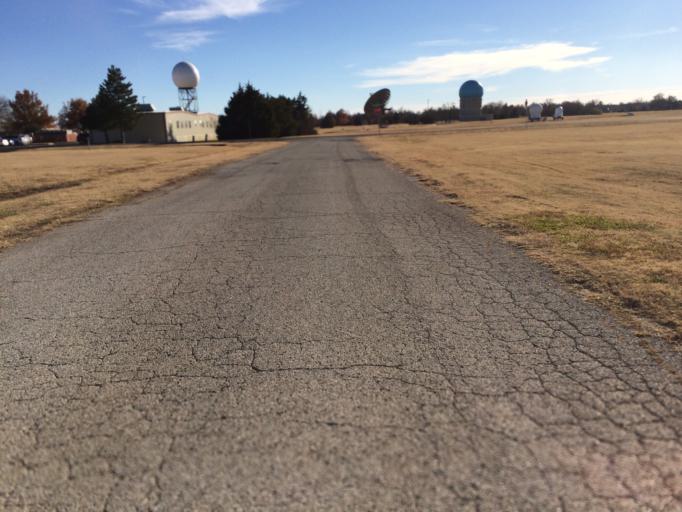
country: US
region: Oklahoma
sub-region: Cleveland County
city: Norman
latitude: 35.2385
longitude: -97.4631
